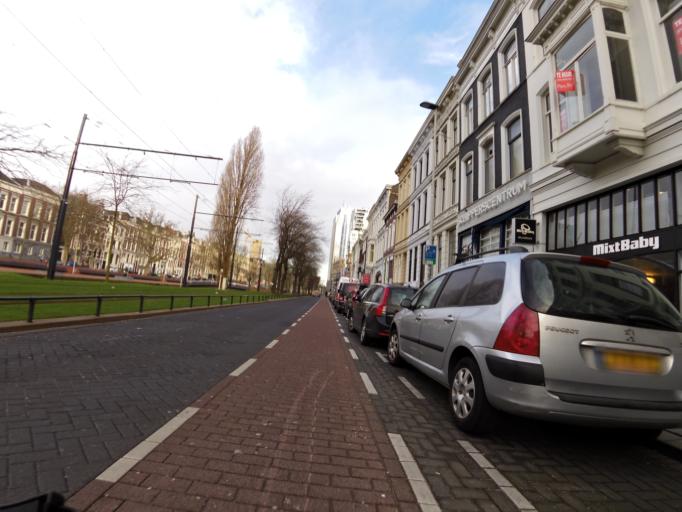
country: NL
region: South Holland
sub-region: Gemeente Rotterdam
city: Rotterdam
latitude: 51.9176
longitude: 4.4728
